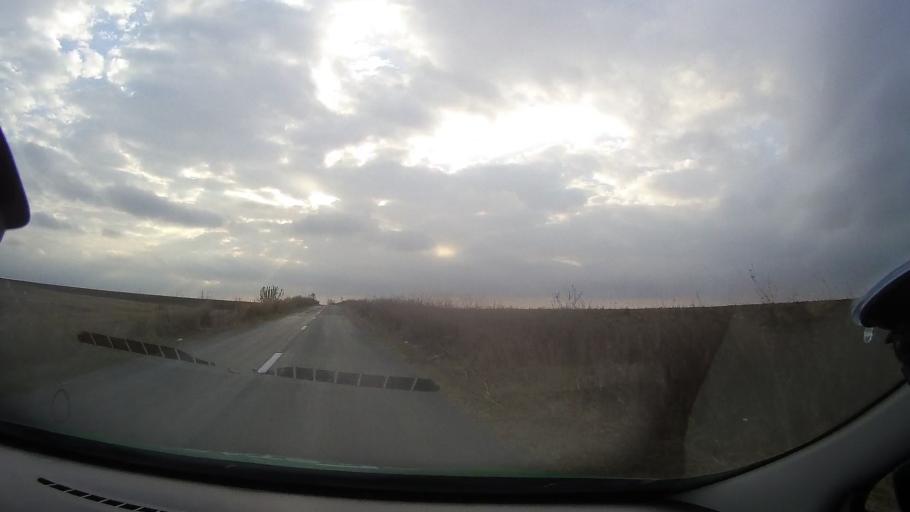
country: RO
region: Constanta
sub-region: Comuna Pestera
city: Pestera
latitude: 44.1321
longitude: 28.1179
